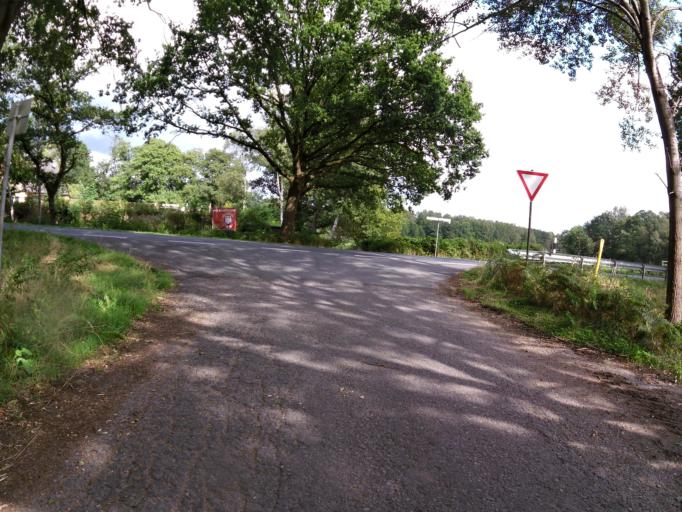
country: DE
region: Lower Saxony
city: Seedorf
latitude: 53.3297
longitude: 9.2550
